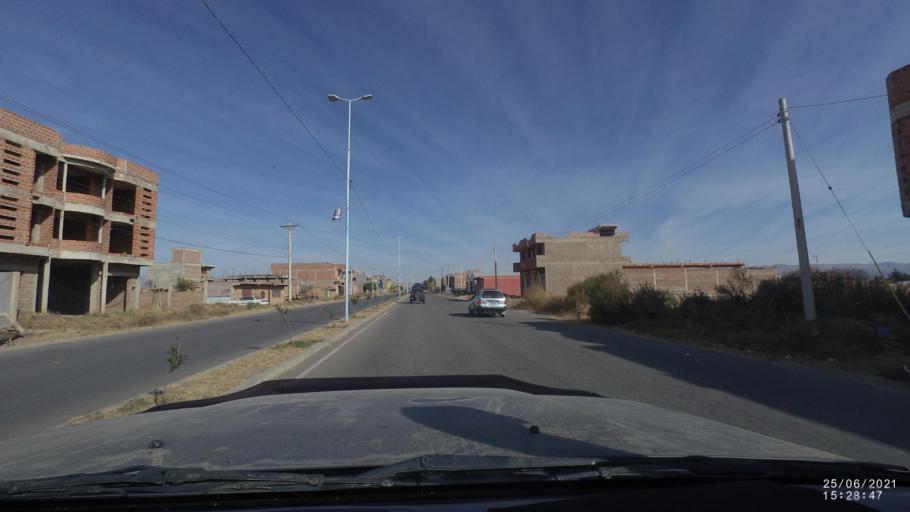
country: BO
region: Cochabamba
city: Cliza
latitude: -17.5638
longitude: -65.9361
